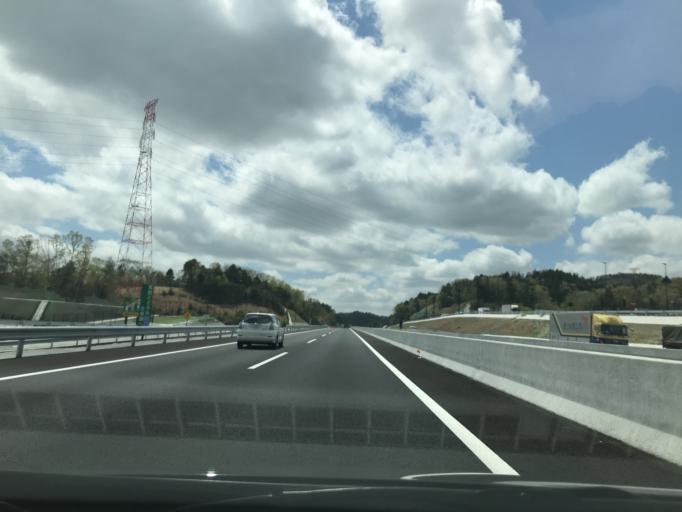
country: JP
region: Osaka
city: Ibaraki
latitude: 34.8816
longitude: 135.5314
